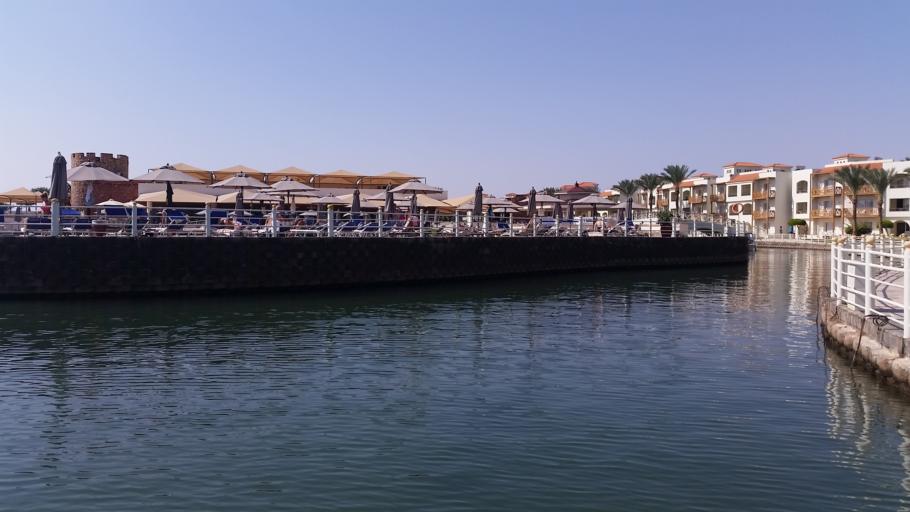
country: EG
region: Red Sea
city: Makadi Bay
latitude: 27.0997
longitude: 33.8339
